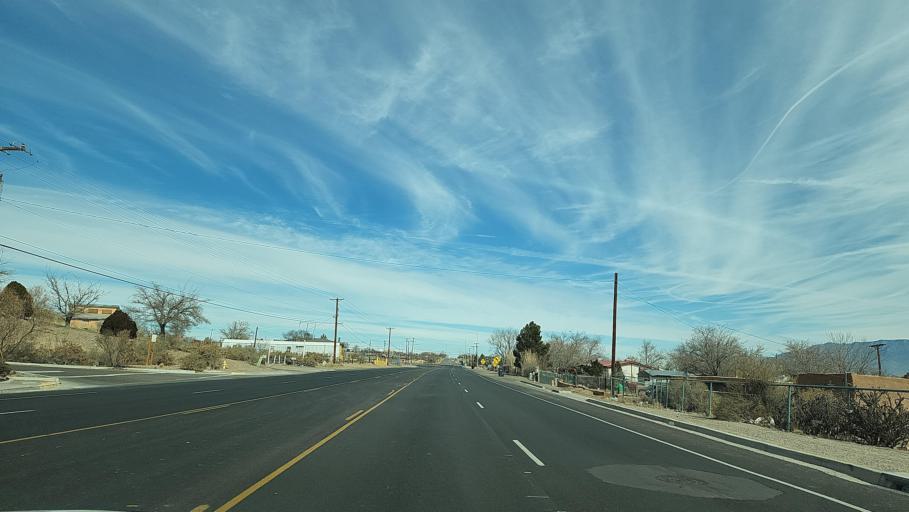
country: US
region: New Mexico
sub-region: Bernalillo County
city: South Valley
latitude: 35.0528
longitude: -106.7066
